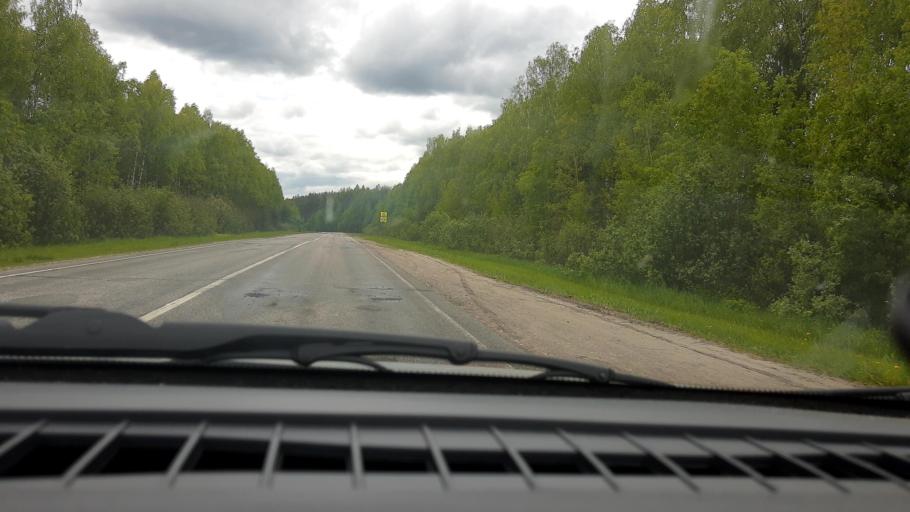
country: RU
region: Nizjnij Novgorod
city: Krasnyye Baki
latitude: 57.0085
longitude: 45.1120
